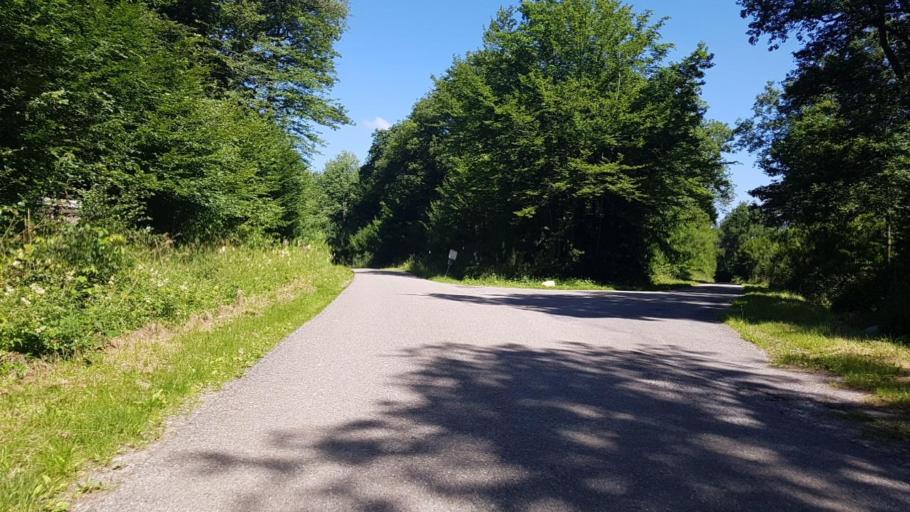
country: BE
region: Wallonia
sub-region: Province du Hainaut
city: Momignies
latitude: 50.0897
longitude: 4.2290
